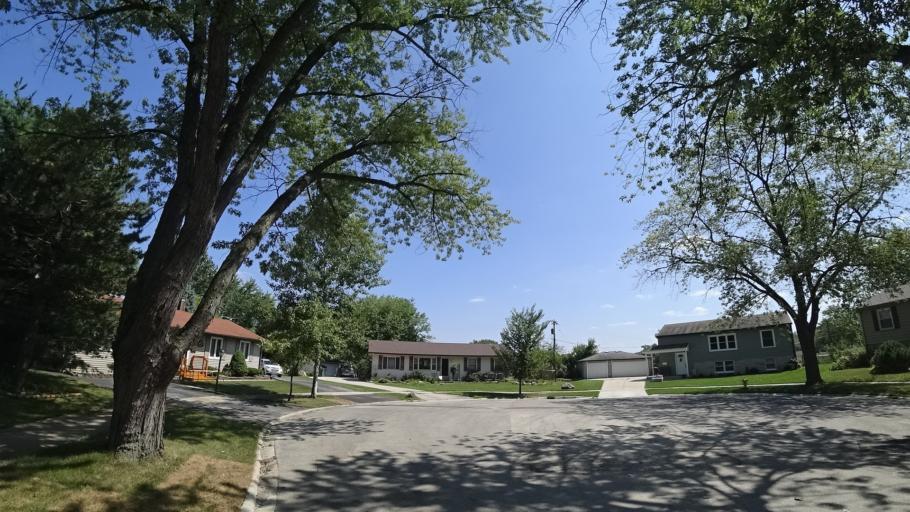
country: US
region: Illinois
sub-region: Cook County
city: Orland Park
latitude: 41.6268
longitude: -87.8407
